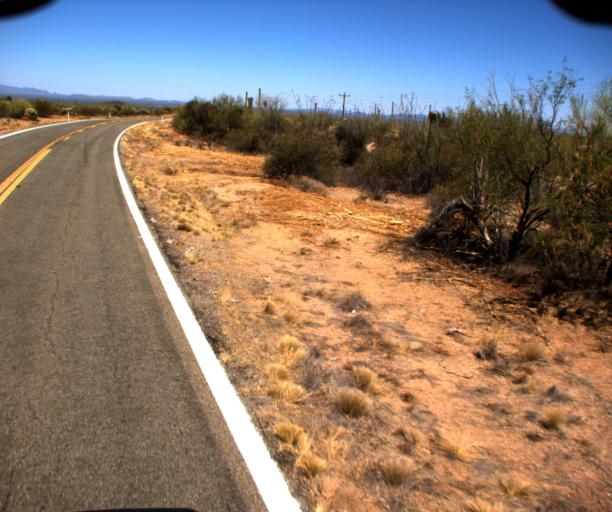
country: US
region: Arizona
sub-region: Pima County
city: Sells
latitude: 32.1764
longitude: -112.2370
